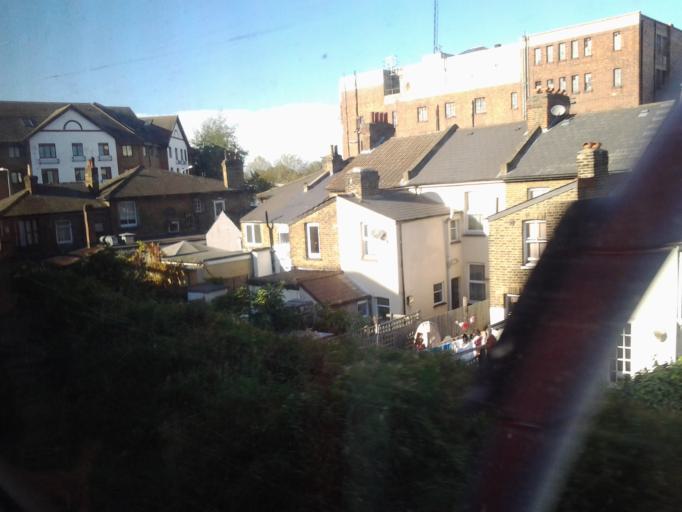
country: GB
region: England
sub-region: Greater London
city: Kingston upon Thames
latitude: 51.4128
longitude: -0.2999
